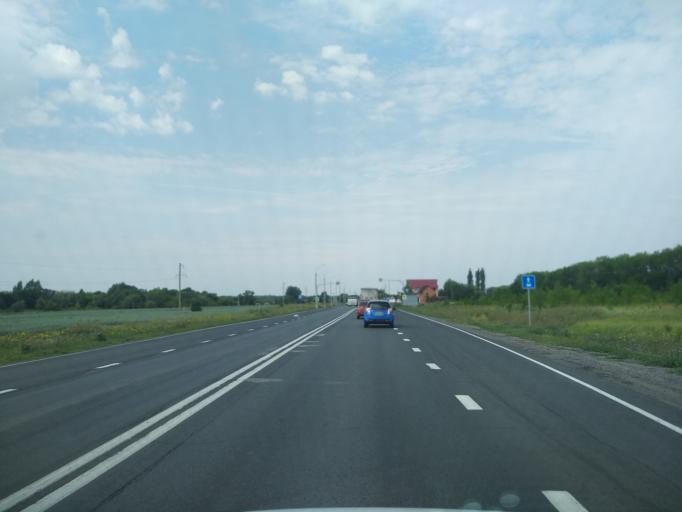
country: RU
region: Voronezj
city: Orlovo
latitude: 51.6797
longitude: 39.6537
